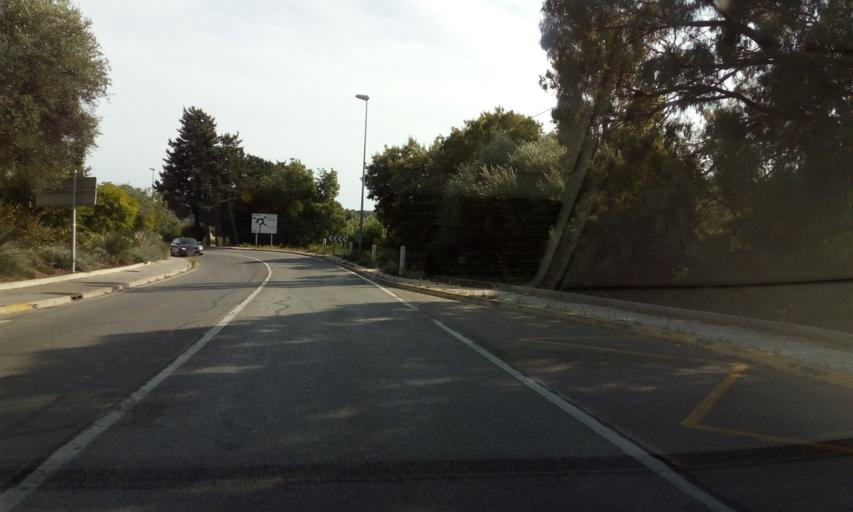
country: FR
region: Provence-Alpes-Cote d'Azur
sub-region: Departement du Var
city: Bormes-les-Mimosas
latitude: 43.1400
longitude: 6.3503
